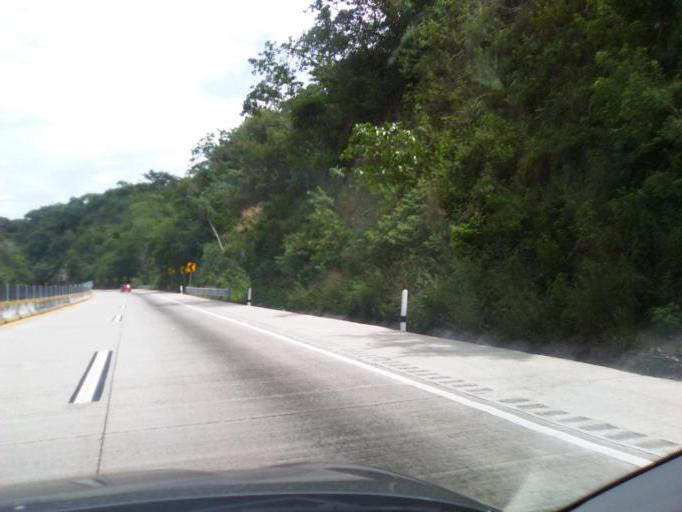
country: MX
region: Guerrero
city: Tierra Colorada
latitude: 17.1906
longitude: -99.5357
